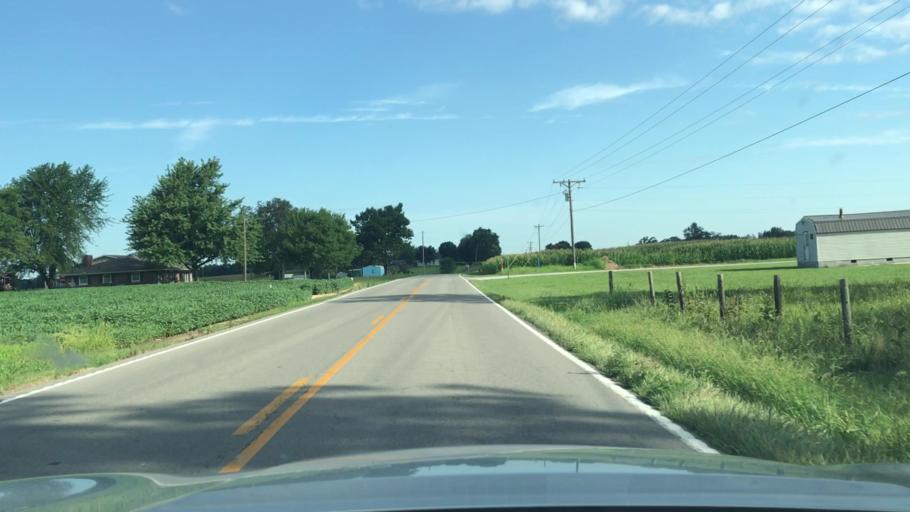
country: US
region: Kentucky
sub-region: Todd County
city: Elkton
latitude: 36.8722
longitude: -87.1653
